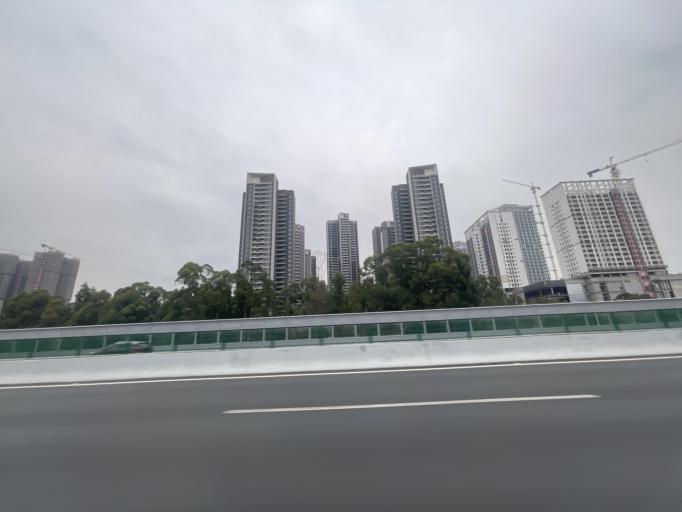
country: CN
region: Guangdong
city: Huangge
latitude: 22.7904
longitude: 113.5119
